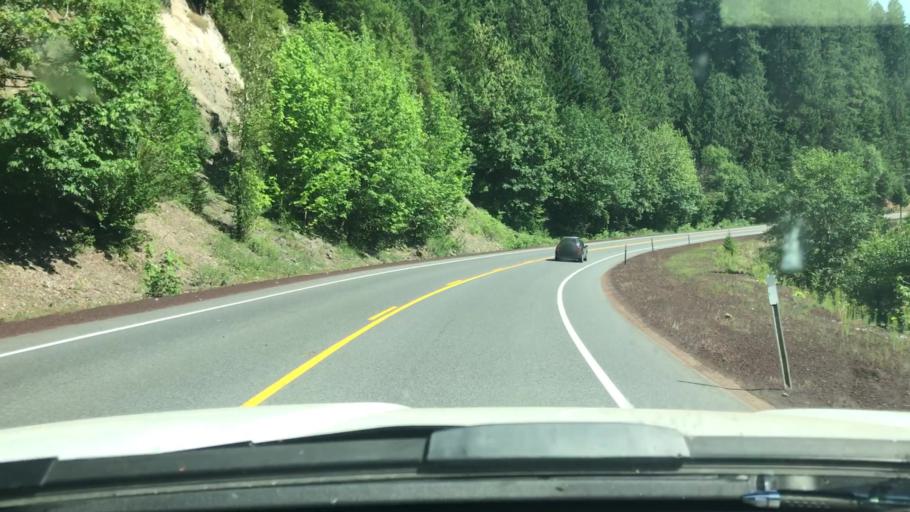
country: US
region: Oregon
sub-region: Deschutes County
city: Sisters
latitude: 44.6364
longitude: -121.9396
